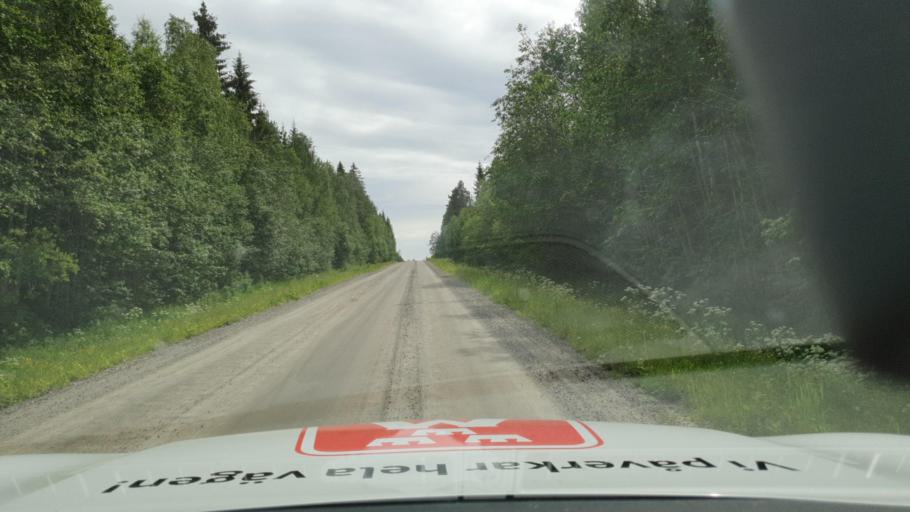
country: SE
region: Vaesterbotten
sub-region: Skelleftea Kommun
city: Burtraesk
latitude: 64.3914
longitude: 20.4132
